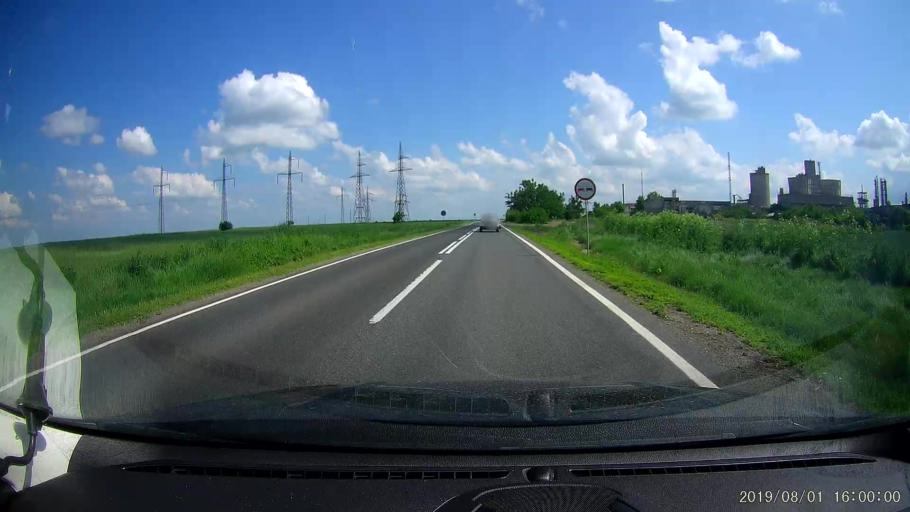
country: RO
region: Ialomita
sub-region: Comuna Slobozia
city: Slobozia
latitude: 44.5370
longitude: 27.3876
